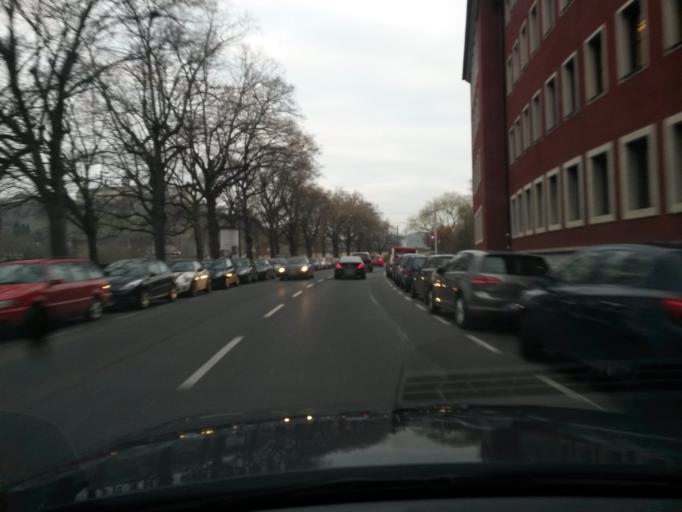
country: DE
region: Bavaria
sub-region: Regierungsbezirk Unterfranken
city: Wuerzburg
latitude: 49.7838
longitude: 9.9285
